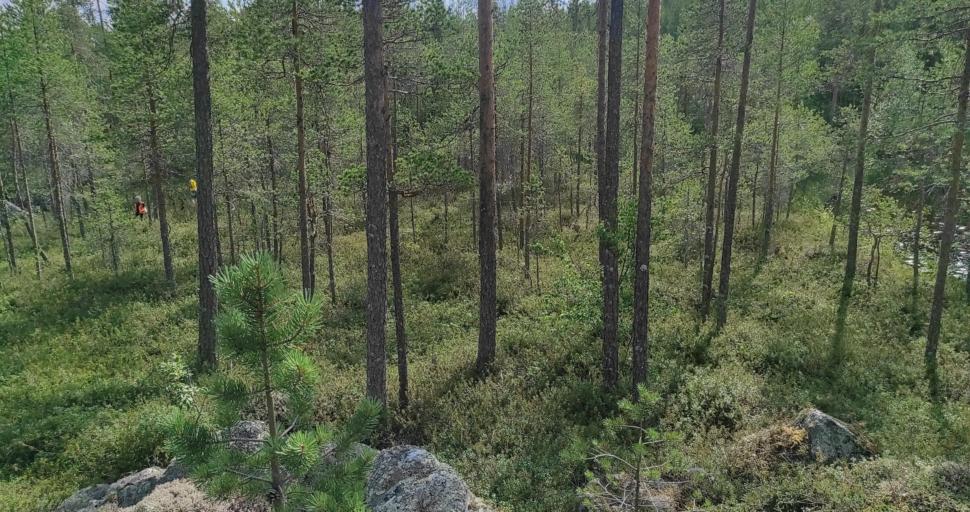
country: RU
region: Murmansk
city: Zelenoborskiy
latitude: 66.6984
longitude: 32.4552
